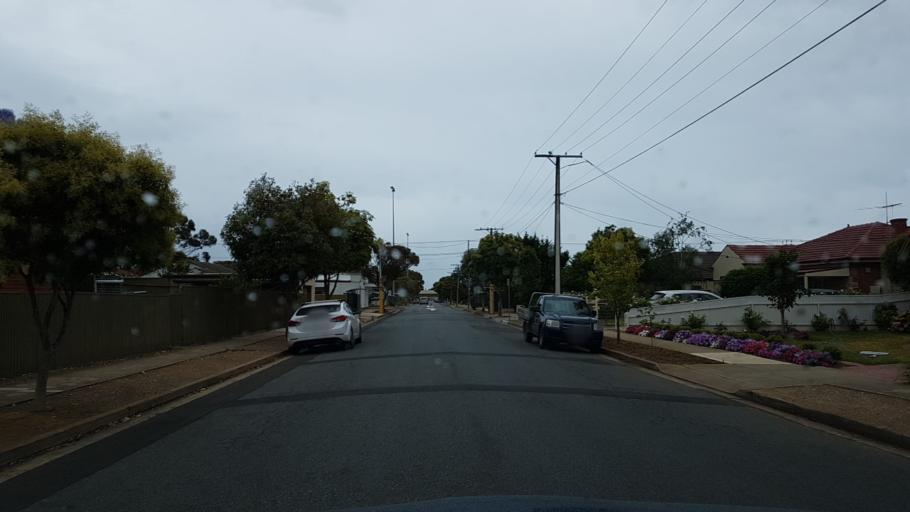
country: AU
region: South Australia
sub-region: Marion
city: South Plympton
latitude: -34.9721
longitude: 138.5500
